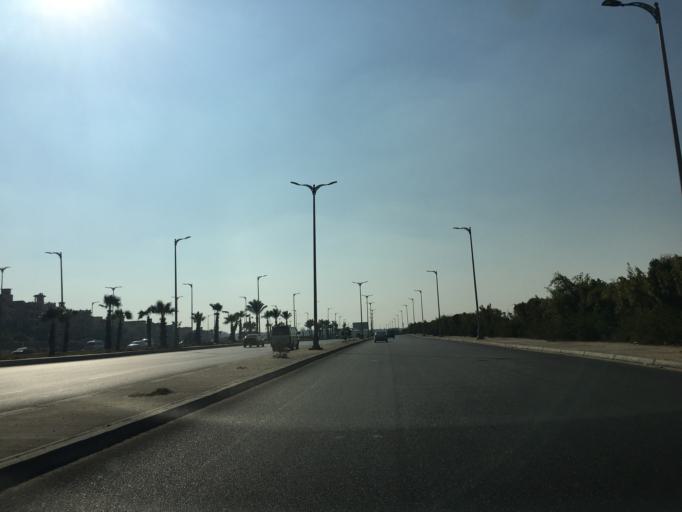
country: EG
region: Al Jizah
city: Madinat Sittah Uktubar
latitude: 29.9929
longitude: 30.9571
